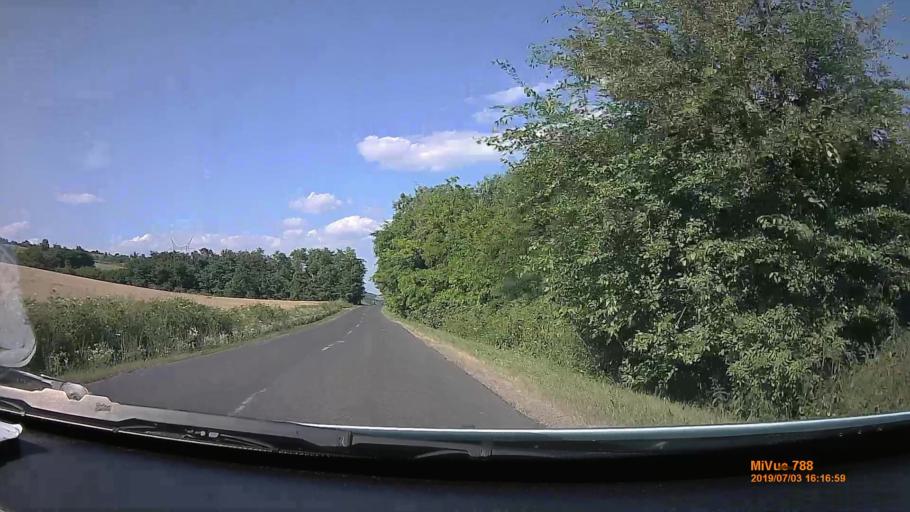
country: HU
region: Borsod-Abauj-Zemplen
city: Putnok
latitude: 48.2139
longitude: 20.4875
